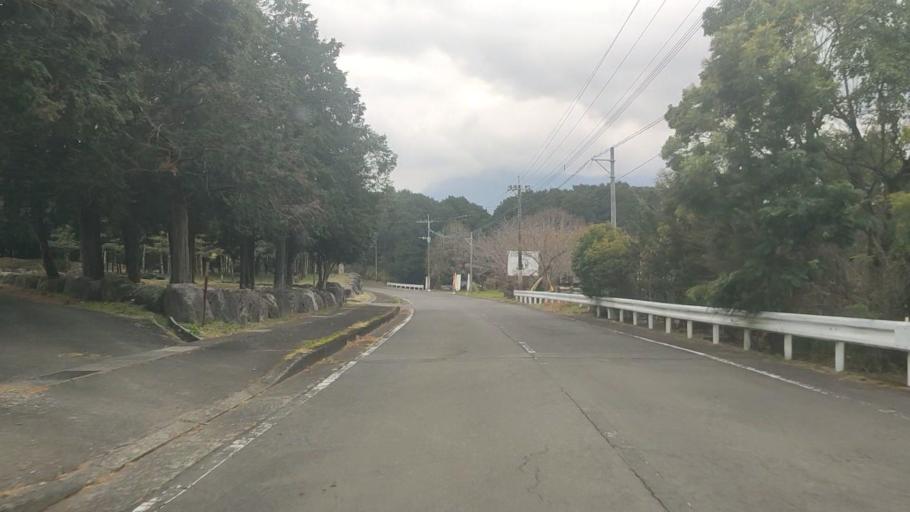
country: JP
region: Nagasaki
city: Shimabara
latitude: 32.8197
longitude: 130.2912
